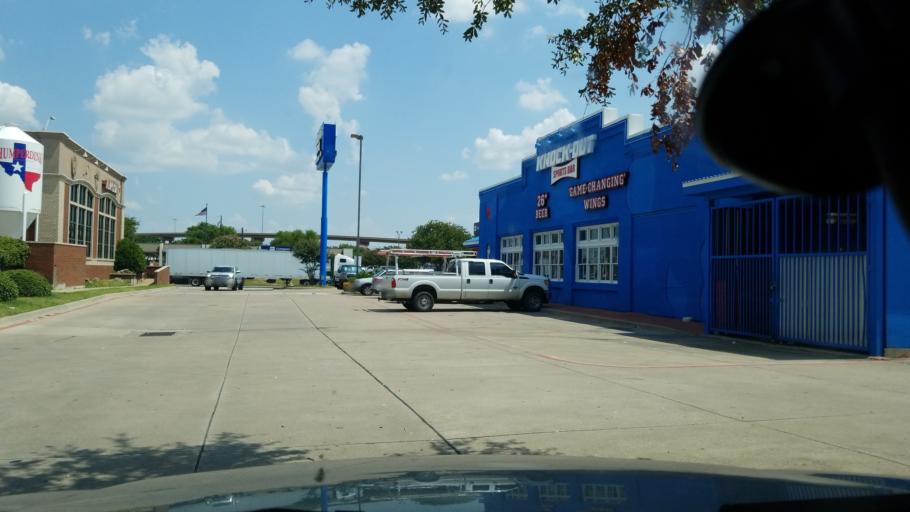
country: US
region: Texas
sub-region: Dallas County
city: Farmers Branch
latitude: 32.8634
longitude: -96.8989
